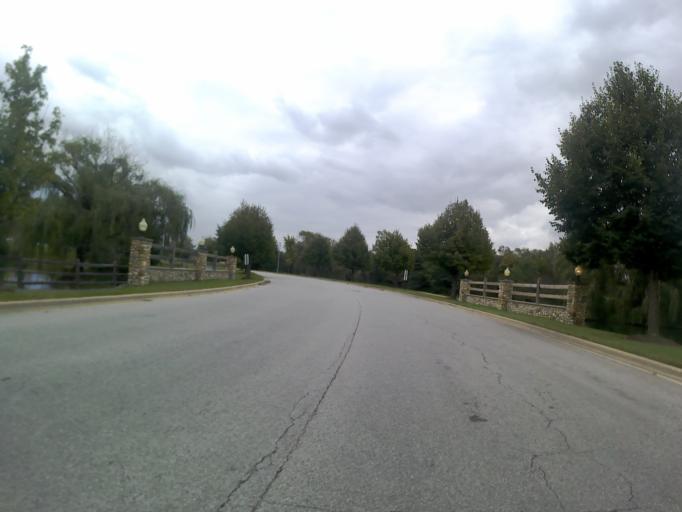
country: US
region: Illinois
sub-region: Kendall County
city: Oswego
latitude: 41.6860
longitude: -88.3605
